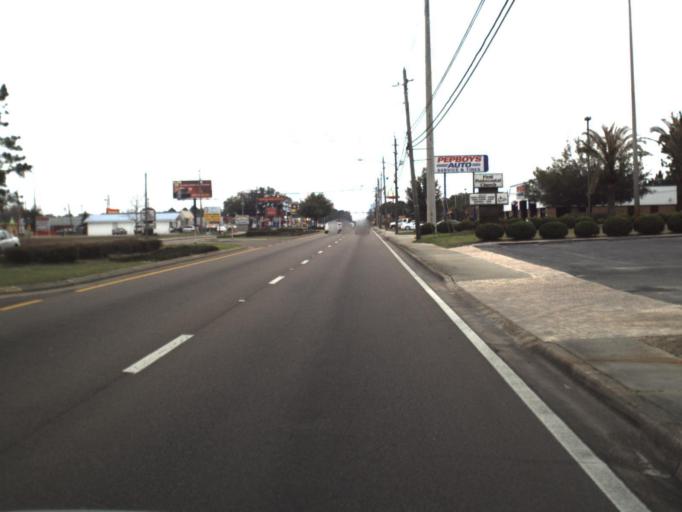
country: US
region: Florida
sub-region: Bay County
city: Springfield
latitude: 30.1493
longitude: -85.5913
